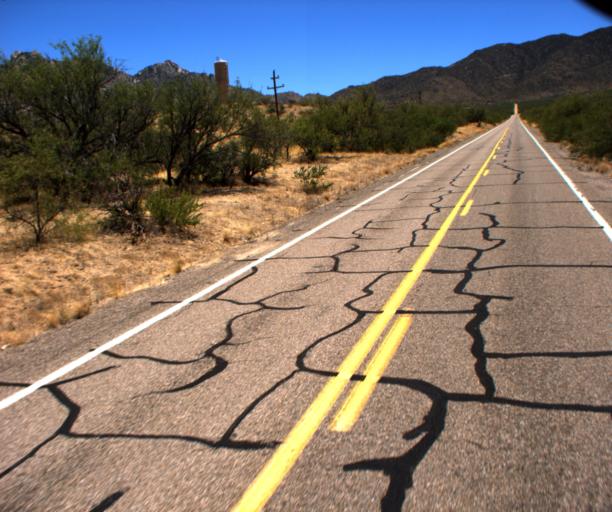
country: US
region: Arizona
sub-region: Pima County
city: Three Points
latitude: 32.0067
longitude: -111.5737
